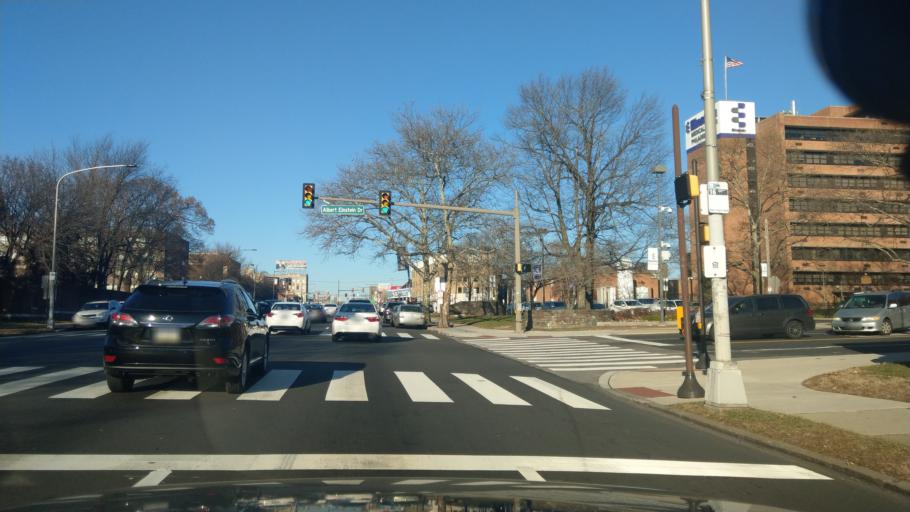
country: US
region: Pennsylvania
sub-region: Montgomery County
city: Wyncote
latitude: 40.0367
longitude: -75.1451
